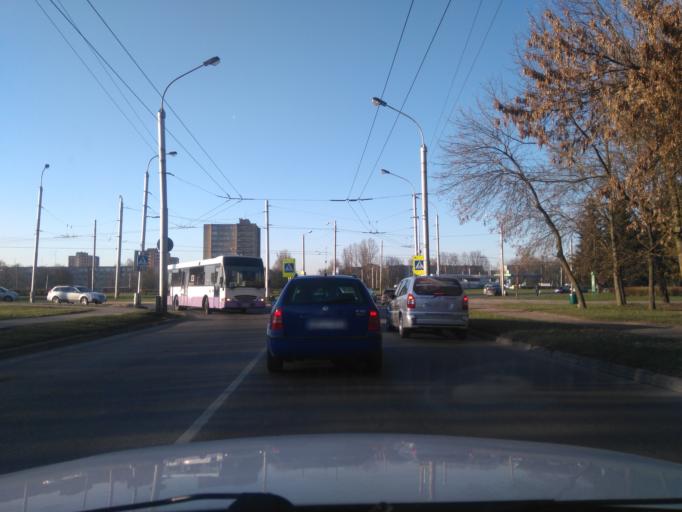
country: LT
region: Kauno apskritis
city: Dainava (Kaunas)
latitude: 54.9139
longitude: 23.9739
